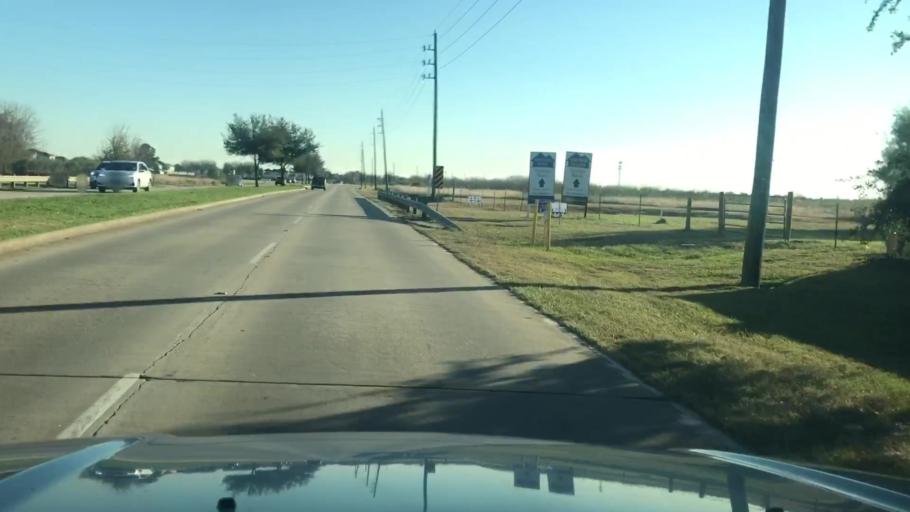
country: US
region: Texas
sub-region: Fort Bend County
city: Cinco Ranch
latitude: 29.8400
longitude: -95.7189
